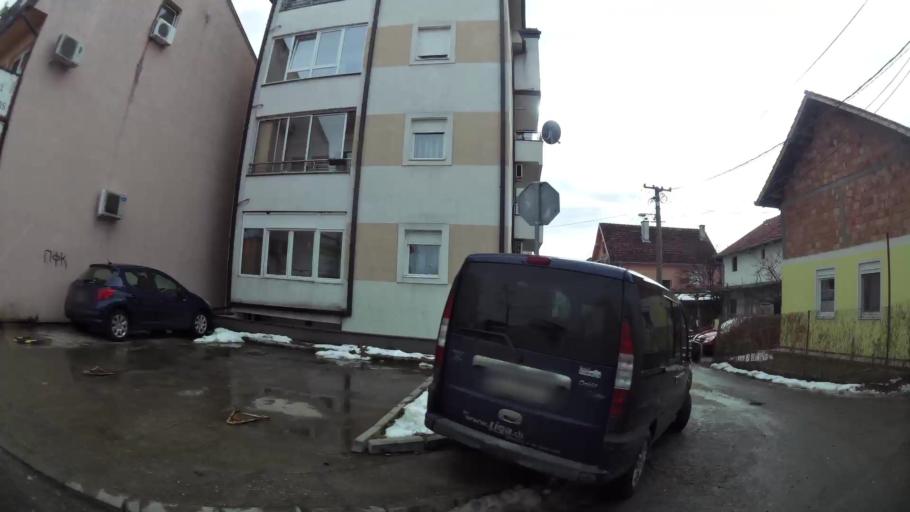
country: RS
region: Central Serbia
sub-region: Belgrade
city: Zemun
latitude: 44.8047
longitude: 20.3555
